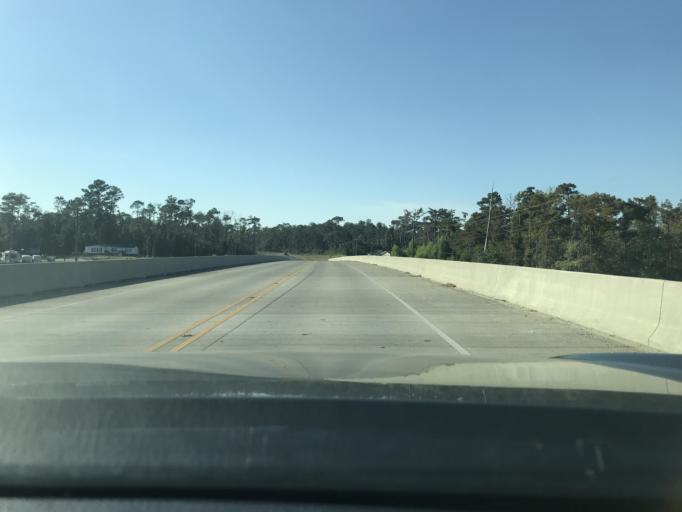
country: US
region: Louisiana
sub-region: Calcasieu Parish
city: Moss Bluff
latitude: 30.3029
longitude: -93.2475
